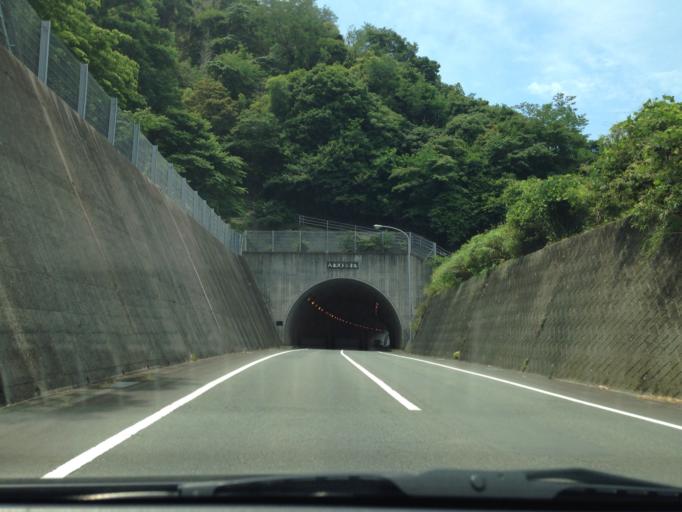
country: JP
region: Shizuoka
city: Heda
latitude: 34.8976
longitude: 138.7790
